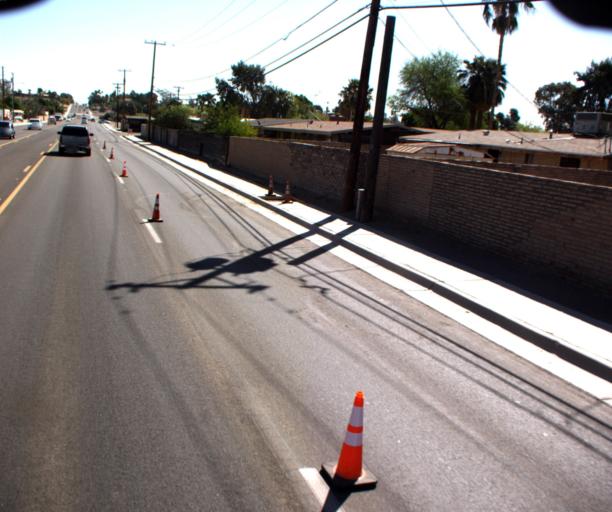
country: US
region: Arizona
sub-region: Yuma County
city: Yuma
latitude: 32.6985
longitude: -114.6477
